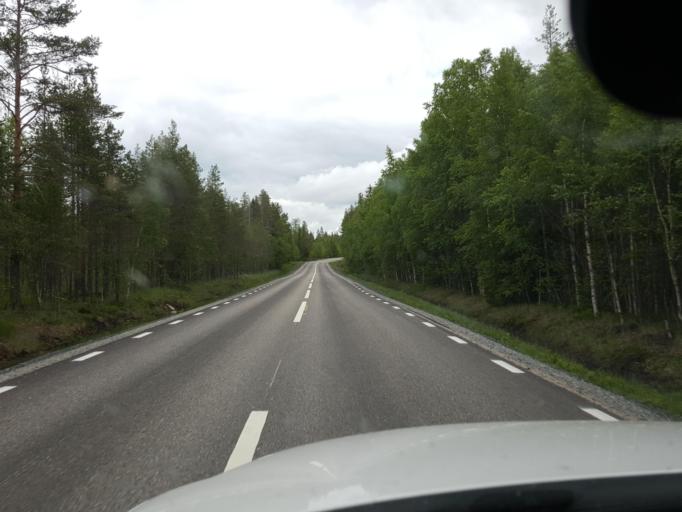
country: SE
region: Gaevleborg
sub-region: Ljusdals Kommun
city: Farila
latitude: 61.7463
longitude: 15.3607
